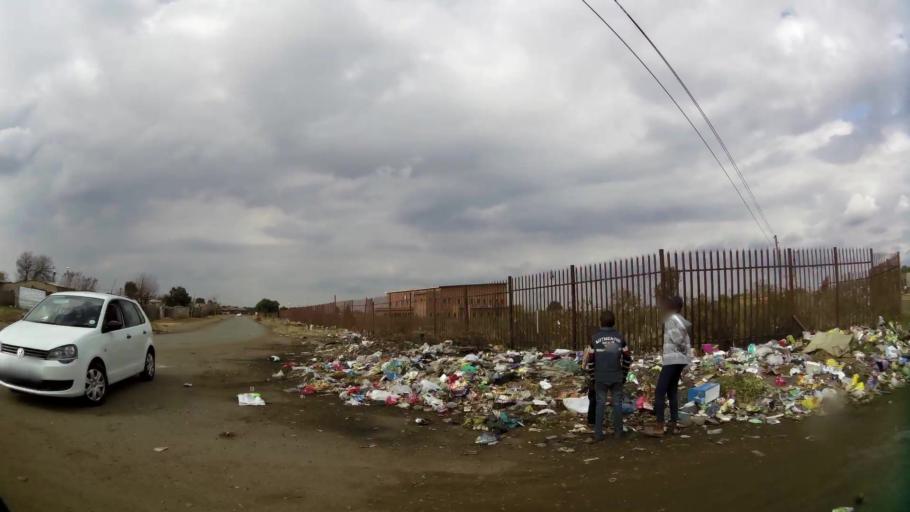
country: ZA
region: Gauteng
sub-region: Sedibeng District Municipality
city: Vanderbijlpark
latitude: -26.6993
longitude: 27.7913
